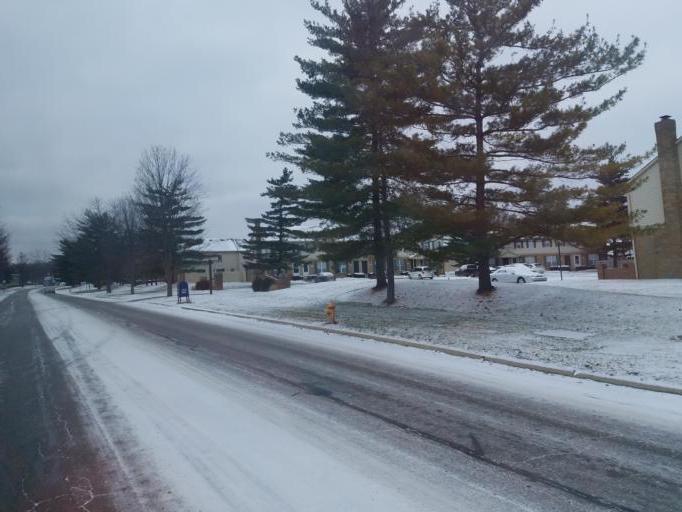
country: US
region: Ohio
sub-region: Delaware County
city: Powell
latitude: 40.1247
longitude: -83.0866
